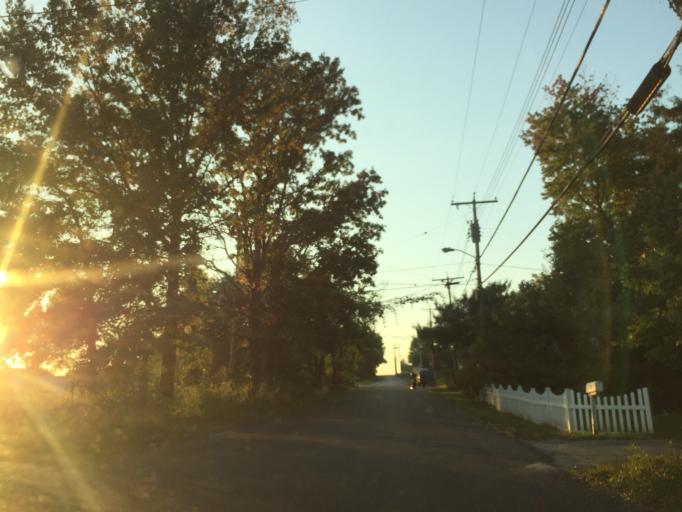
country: US
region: Maryland
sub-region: Baltimore County
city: Essex
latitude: 39.3173
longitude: -76.4600
